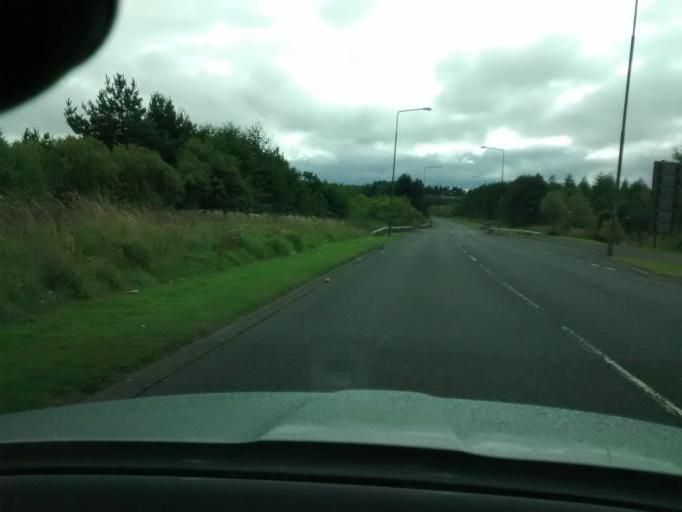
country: GB
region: Scotland
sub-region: West Lothian
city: West Calder
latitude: 55.8938
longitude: -3.5673
